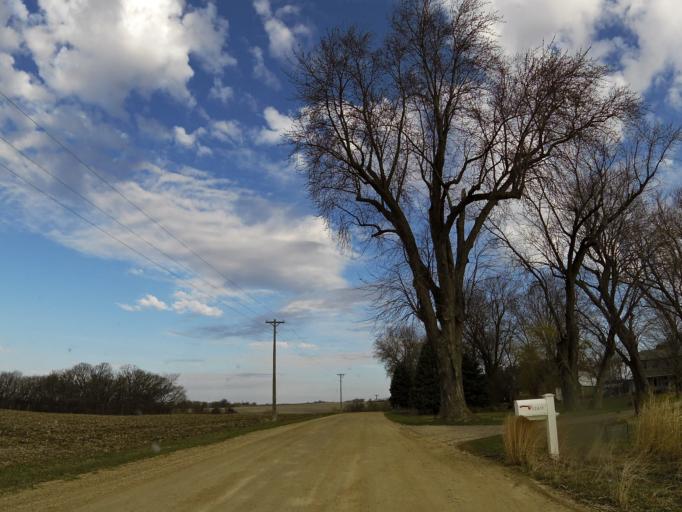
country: US
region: Minnesota
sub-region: Dakota County
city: Hastings
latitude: 44.7629
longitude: -92.8340
